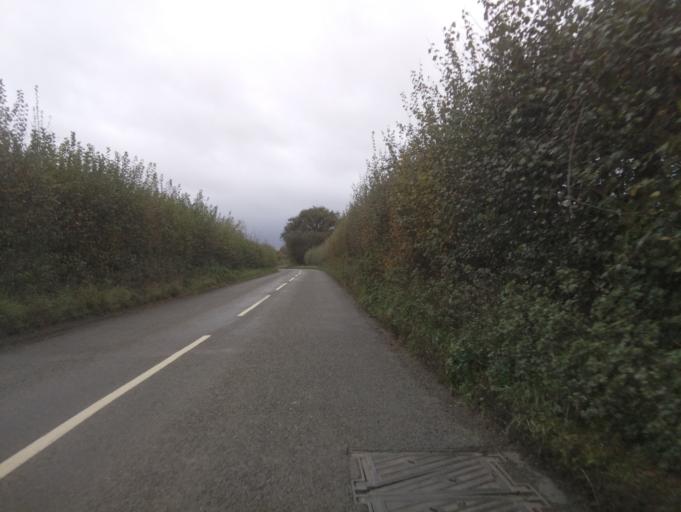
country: GB
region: England
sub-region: Somerset
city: Ilminster
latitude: 50.9526
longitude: -2.9024
